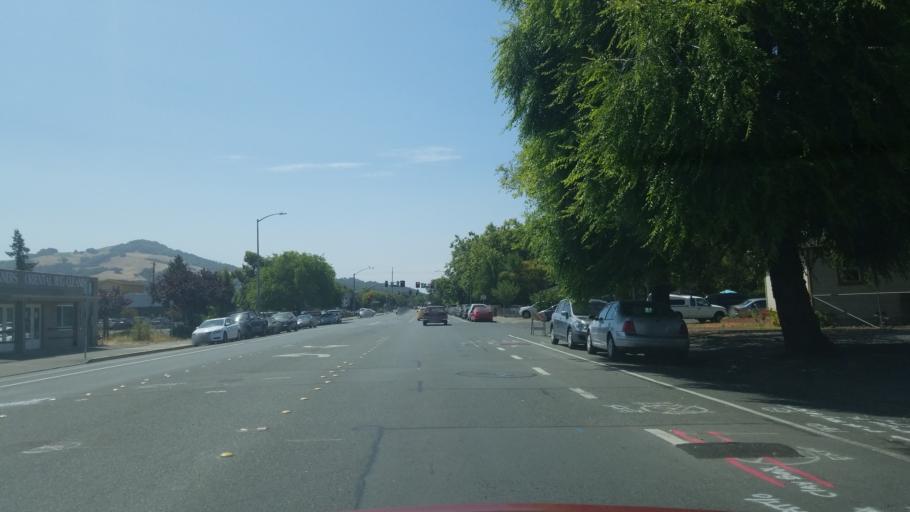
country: US
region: California
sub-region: Sonoma County
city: Santa Rosa
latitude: 38.4252
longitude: -122.7091
